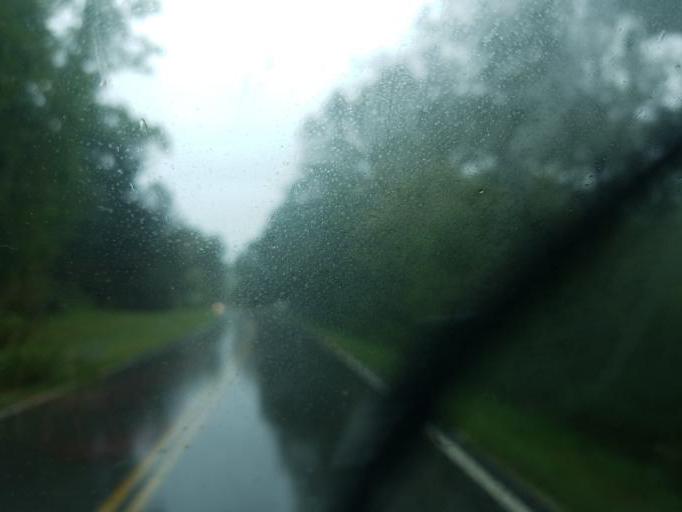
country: US
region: Kentucky
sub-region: Carter County
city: Grayson
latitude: 38.4916
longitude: -83.0222
